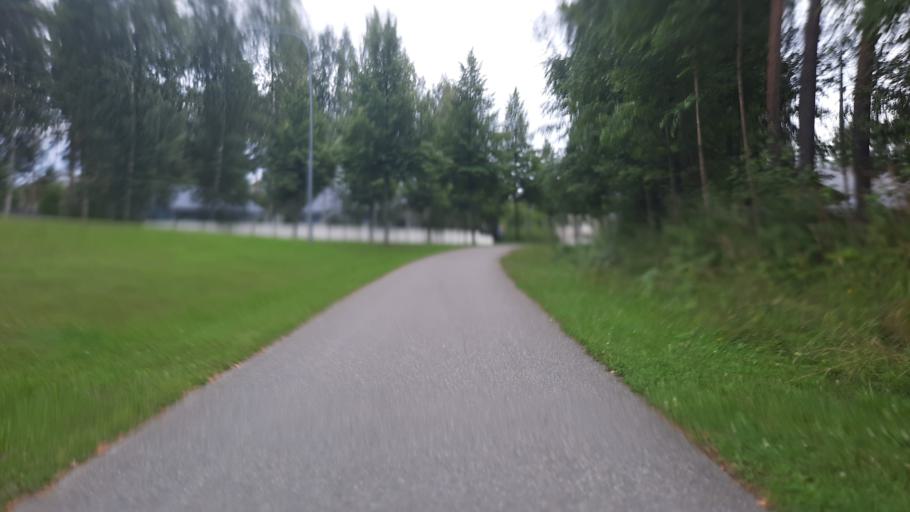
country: FI
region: North Karelia
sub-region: Joensuu
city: Joensuu
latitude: 62.6218
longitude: 29.8577
